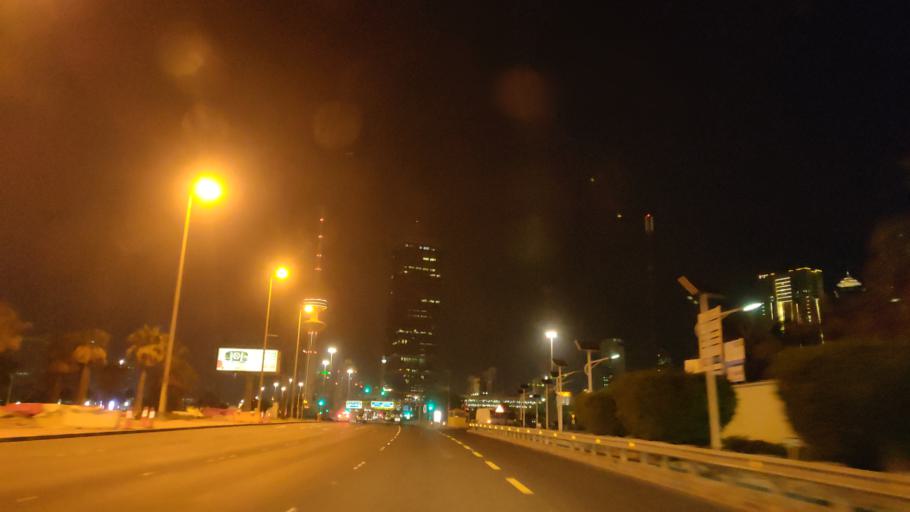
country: KW
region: Al Asimah
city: Kuwait City
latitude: 29.3574
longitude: 47.9746
